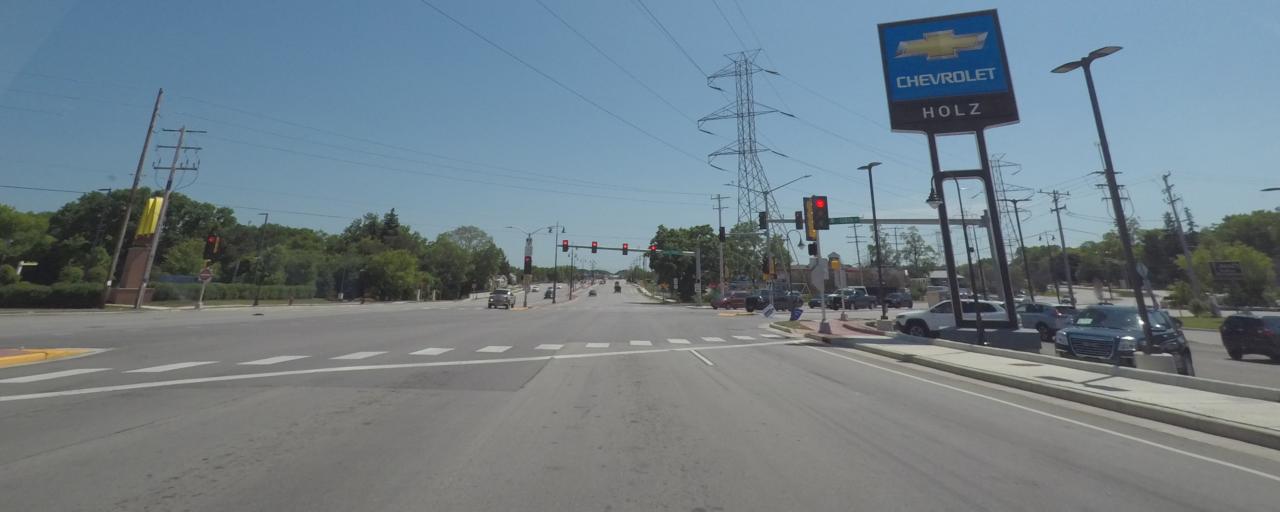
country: US
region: Wisconsin
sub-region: Milwaukee County
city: Hales Corners
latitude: 42.9362
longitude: -88.0486
